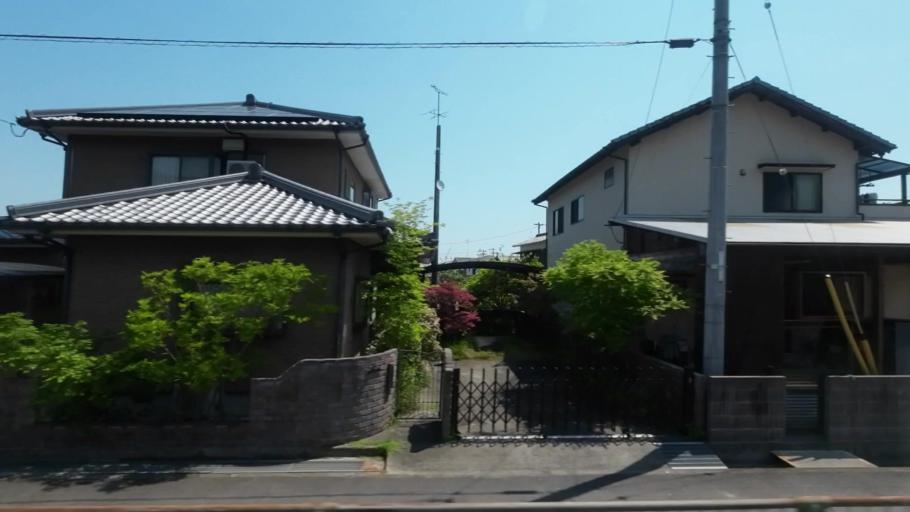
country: JP
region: Ehime
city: Saijo
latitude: 34.0129
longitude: 133.0355
